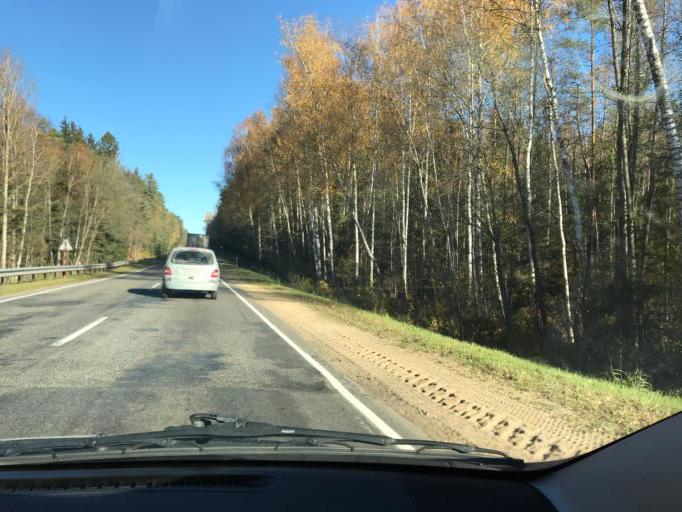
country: BY
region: Vitebsk
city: Polatsk
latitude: 55.3383
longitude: 28.7919
